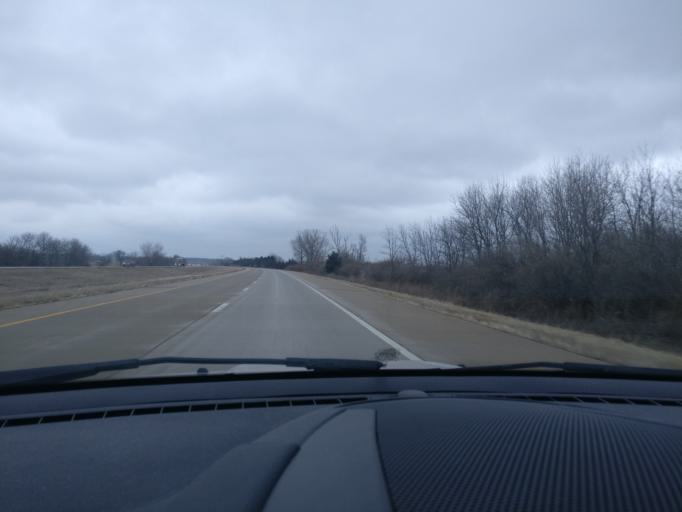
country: US
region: Illinois
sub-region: Whiteside County
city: Prophetstown
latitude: 41.7519
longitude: -89.8617
